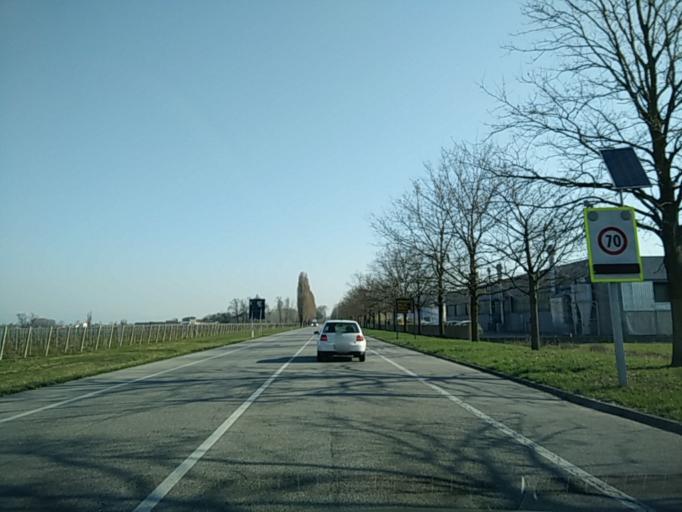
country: IT
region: Friuli Venezia Giulia
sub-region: Provincia di Pordenone
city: Villotta
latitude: 45.8671
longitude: 12.7660
